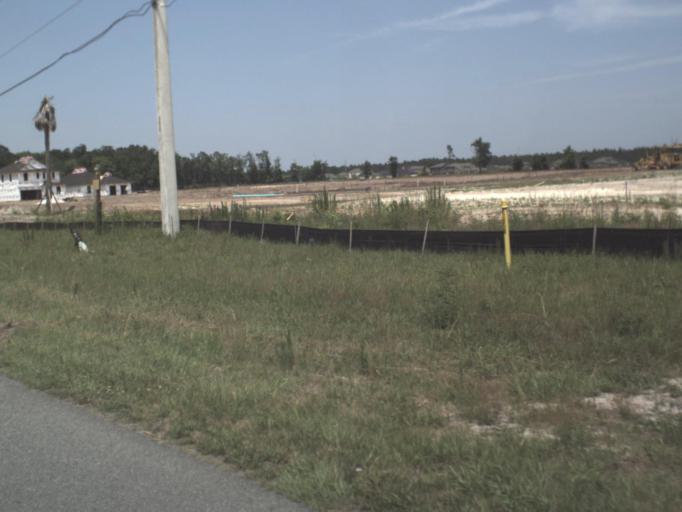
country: US
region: Florida
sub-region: Nassau County
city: Yulee
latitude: 30.5285
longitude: -81.6223
